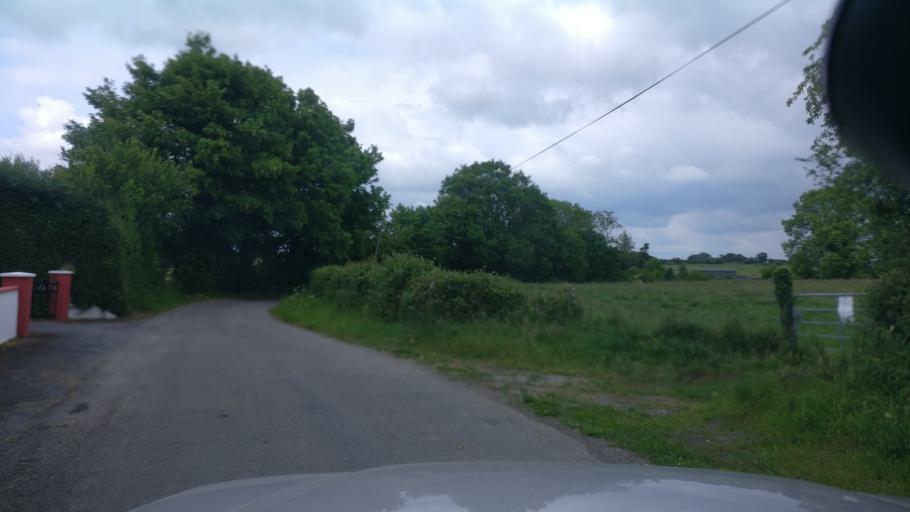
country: IE
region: Connaught
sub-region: County Galway
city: Ballinasloe
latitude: 53.2838
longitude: -8.3170
